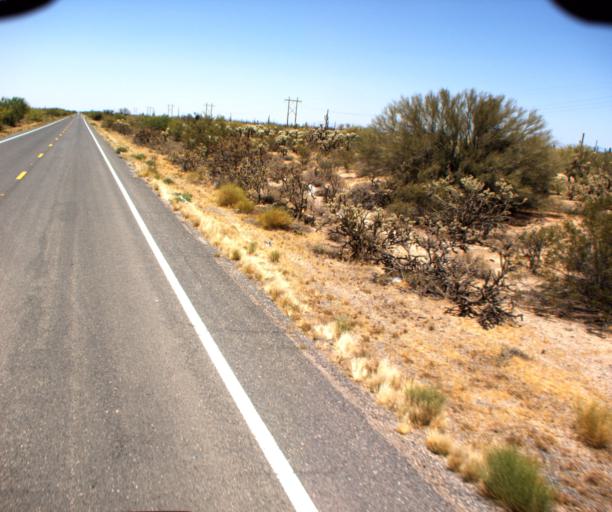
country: US
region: Arizona
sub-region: Pinal County
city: Florence
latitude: 32.8555
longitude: -111.2355
